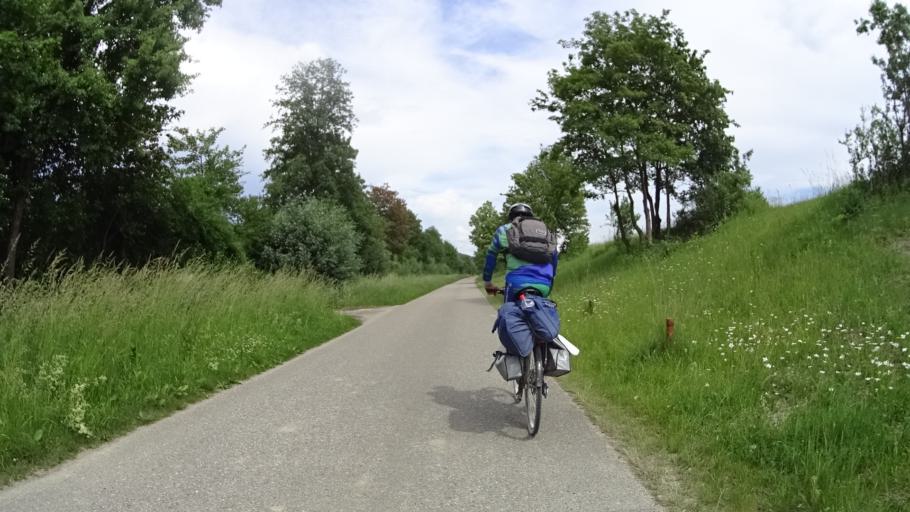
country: DE
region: Bavaria
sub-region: Upper Palatinate
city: Wiesent
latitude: 49.0166
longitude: 12.3027
